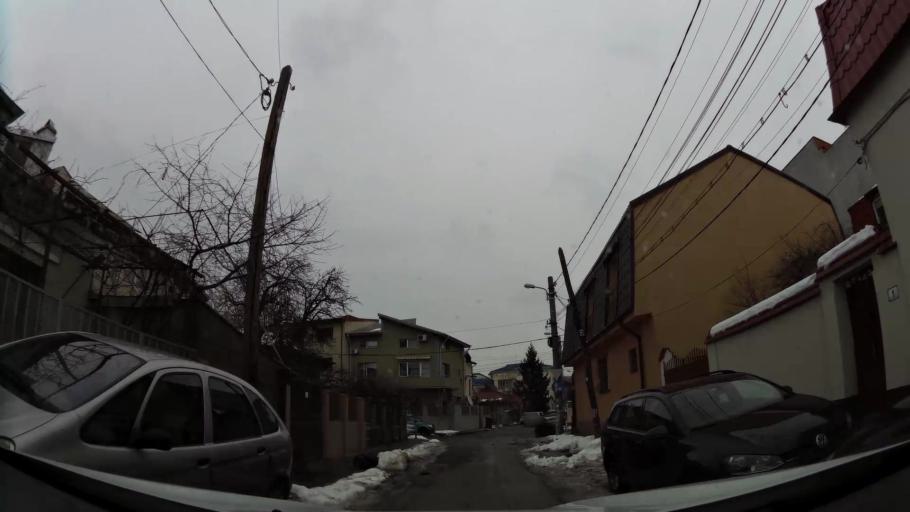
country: RO
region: Bucuresti
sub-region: Municipiul Bucuresti
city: Bucuresti
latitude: 44.4209
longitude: 26.0573
